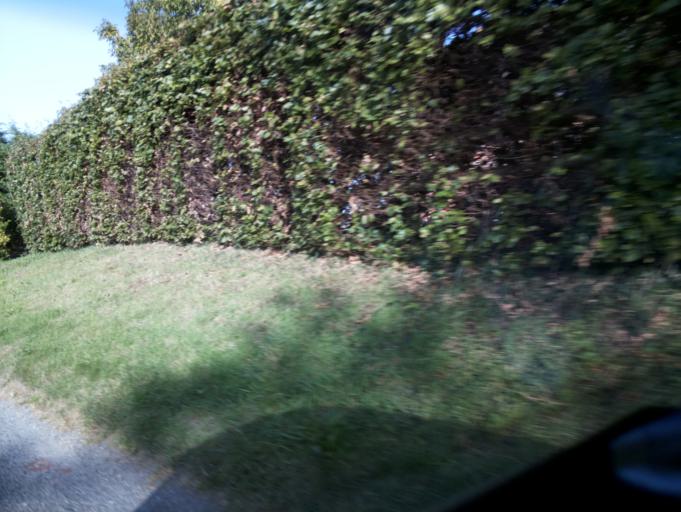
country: GB
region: England
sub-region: Gloucestershire
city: Tewkesbury
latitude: 51.9513
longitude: -2.1937
